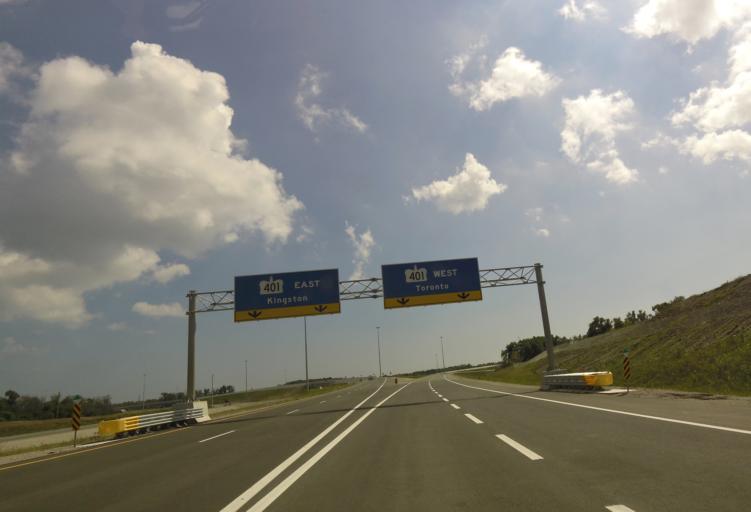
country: CA
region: Ontario
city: Ajax
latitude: 43.8711
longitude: -78.9761
